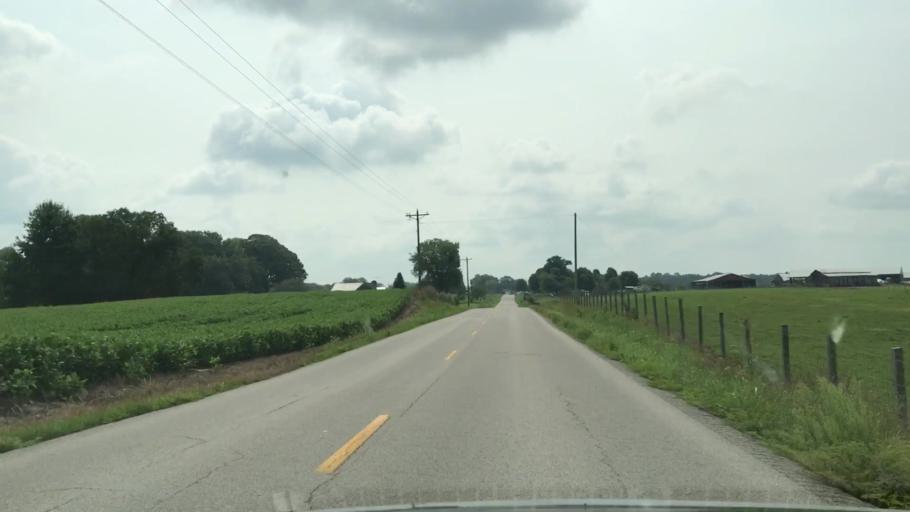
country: US
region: Kentucky
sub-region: Edmonson County
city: Brownsville
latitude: 37.1384
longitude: -86.1787
